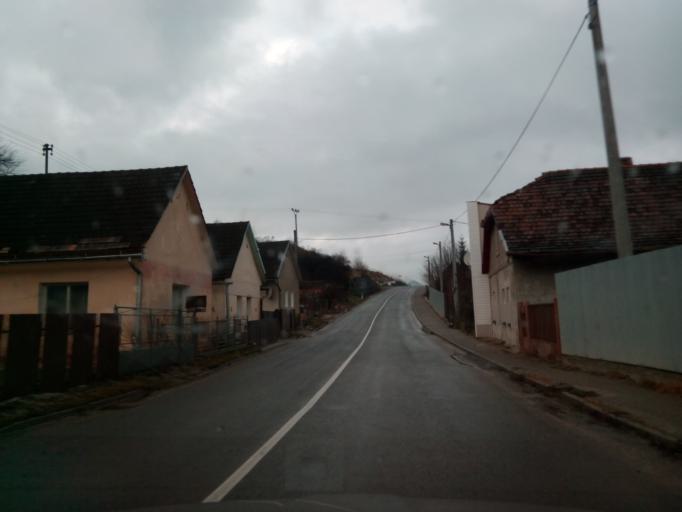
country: SK
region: Kosicky
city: Gelnica
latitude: 48.8575
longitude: 21.0125
